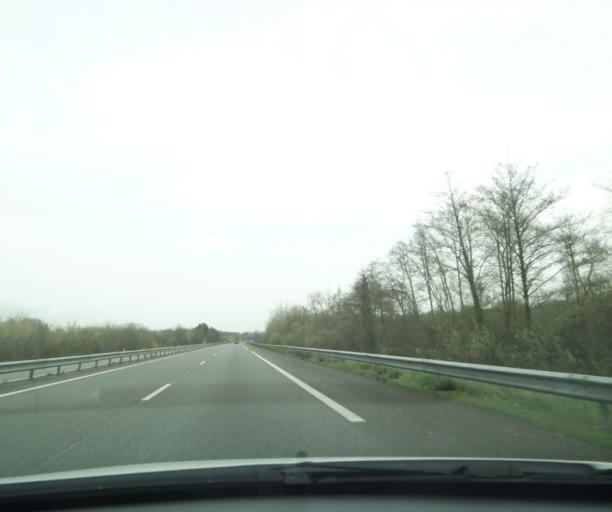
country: FR
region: Aquitaine
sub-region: Departement des Pyrenees-Atlantiques
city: Bidache
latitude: 43.5314
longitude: -1.1728
